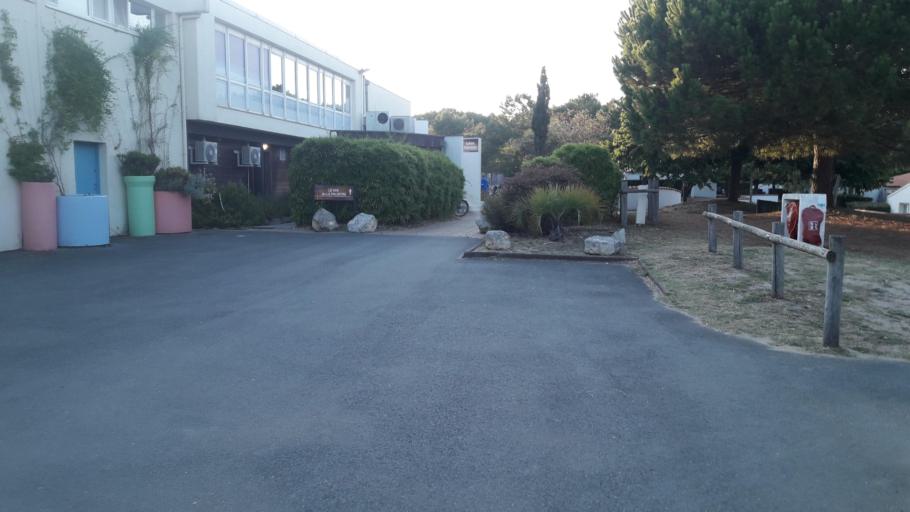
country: FR
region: Poitou-Charentes
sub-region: Departement de la Charente-Maritime
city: Les Mathes
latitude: 45.6887
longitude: -1.1888
